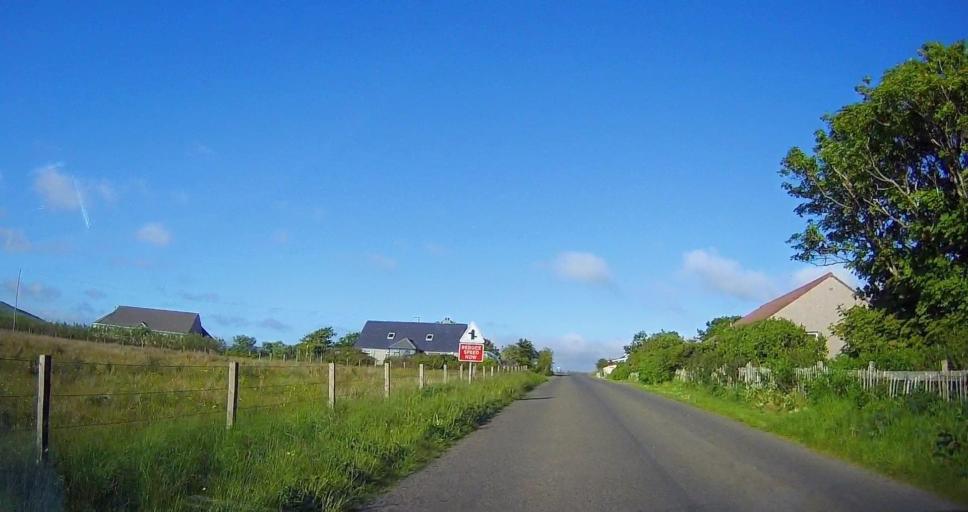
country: GB
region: Scotland
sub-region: Orkney Islands
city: Stromness
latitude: 59.0724
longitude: -3.2232
